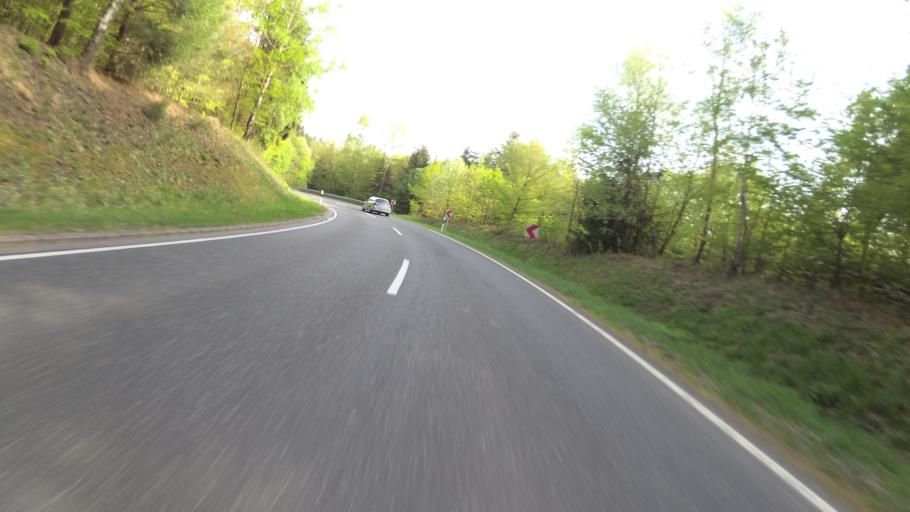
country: DE
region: Rheinland-Pfalz
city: Bausendorf
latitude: 50.0348
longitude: 6.9932
